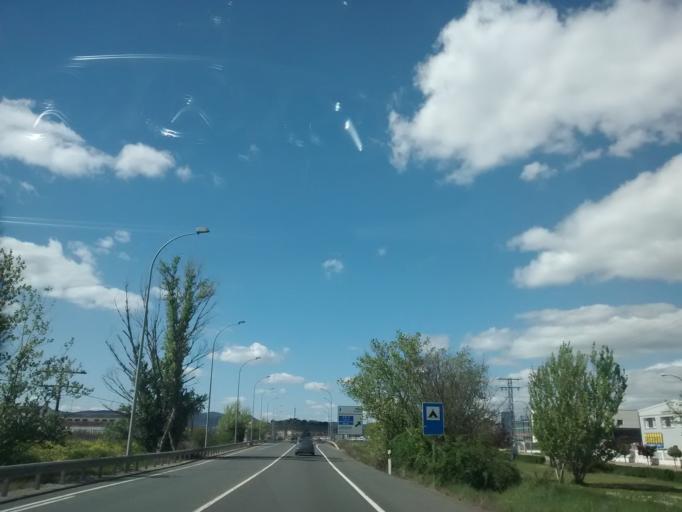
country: ES
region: La Rioja
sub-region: Provincia de La Rioja
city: Ollauri
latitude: 42.5590
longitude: -2.8370
